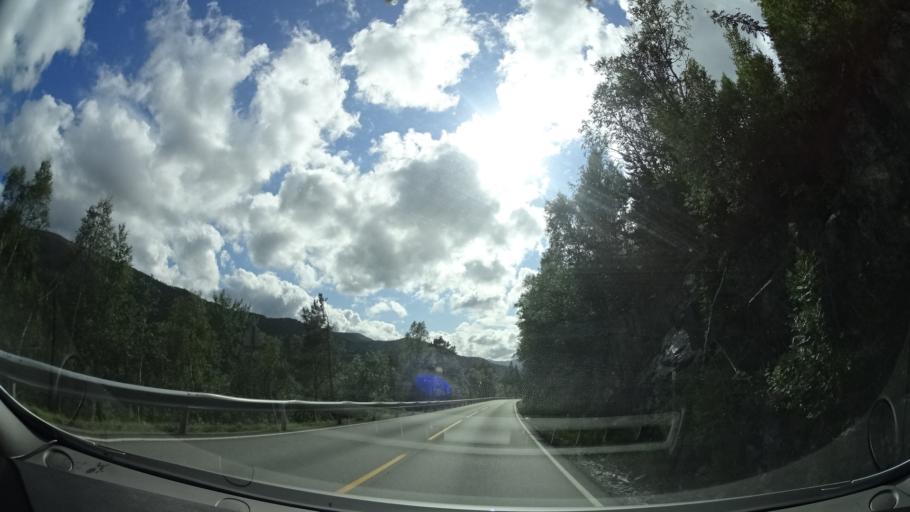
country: NO
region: Sor-Trondelag
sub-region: Hemne
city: Kyrksaeterora
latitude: 63.2127
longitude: 9.1047
